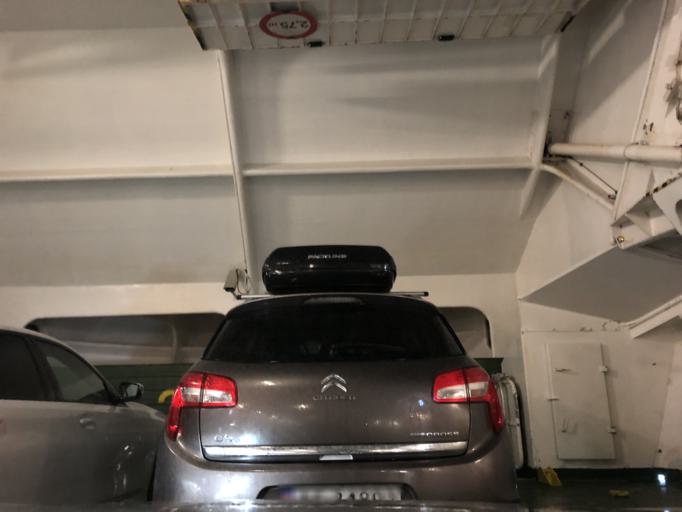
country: NO
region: Rogaland
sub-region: Hjelmeland
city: Hjelmelandsvagen
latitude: 59.2393
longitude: 6.1639
